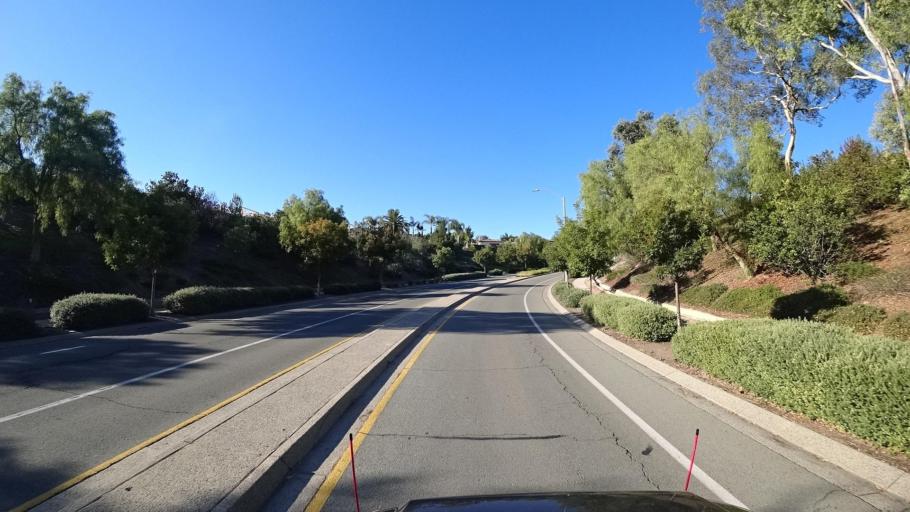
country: US
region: California
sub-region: San Diego County
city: La Presa
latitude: 32.6597
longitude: -116.9420
